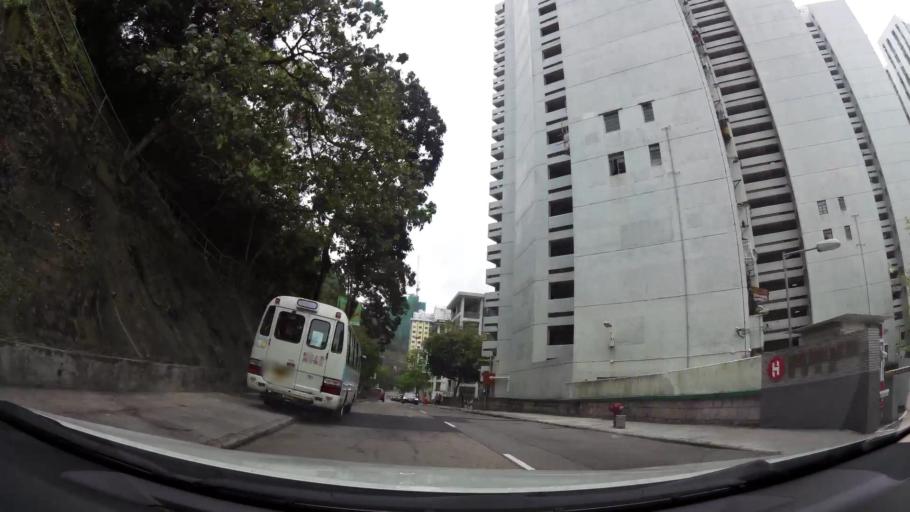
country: HK
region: Wanchai
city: Wan Chai
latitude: 22.2798
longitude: 114.2313
